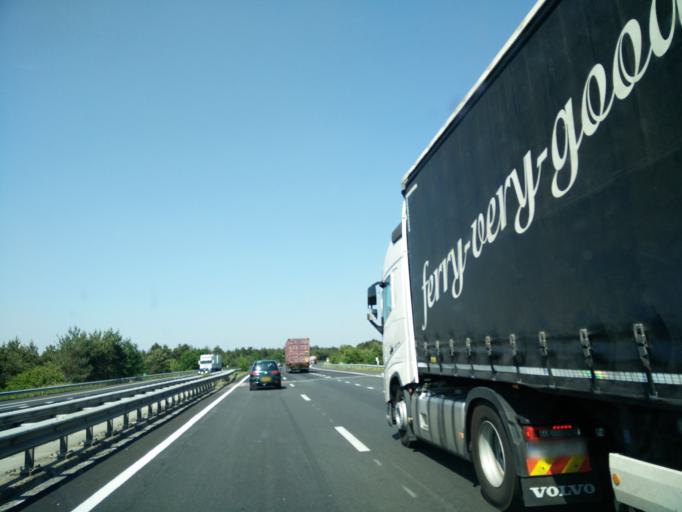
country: NL
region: Gelderland
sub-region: Gemeente Nunspeet
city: Nunspeet
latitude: 52.3792
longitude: 5.8252
